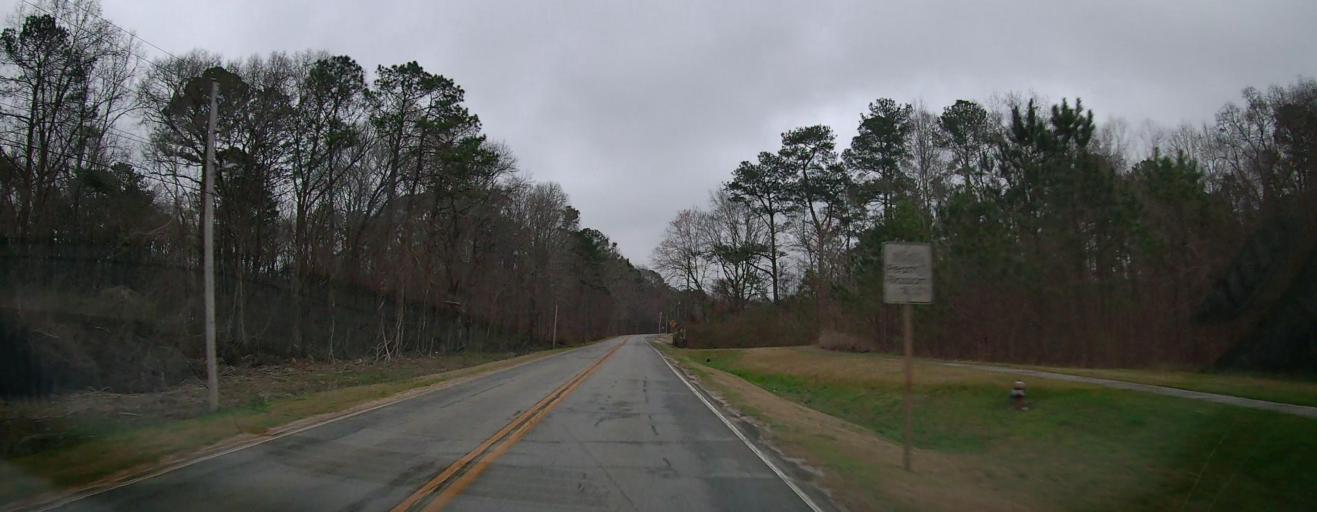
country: US
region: Georgia
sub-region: Lamar County
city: Barnesville
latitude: 33.0543
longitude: -84.1389
